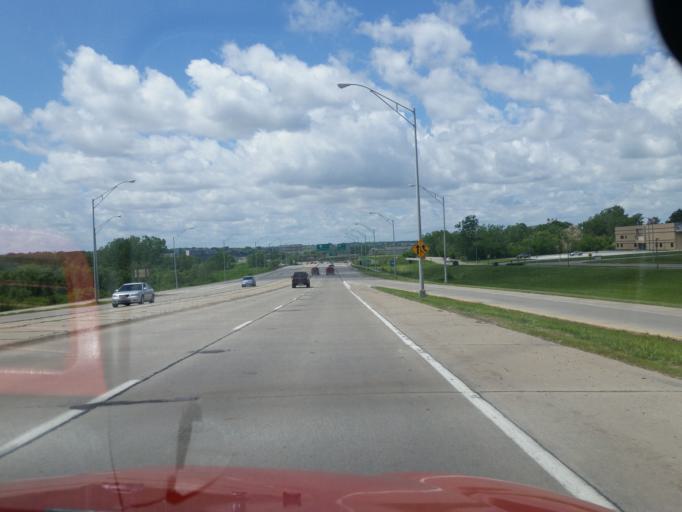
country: US
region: Nebraska
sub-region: Sarpy County
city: Offutt Air Force Base
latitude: 41.1403
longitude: -95.9292
